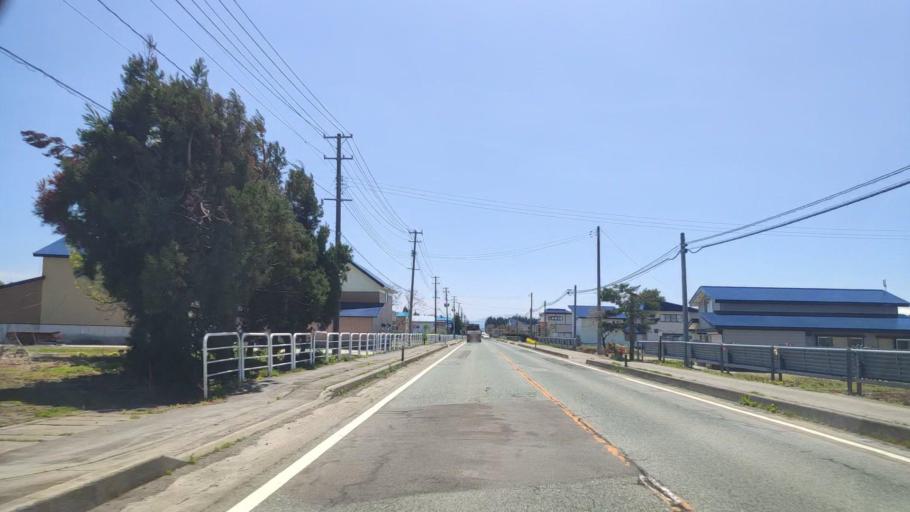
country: JP
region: Yamagata
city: Shinjo
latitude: 38.8308
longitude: 140.3283
